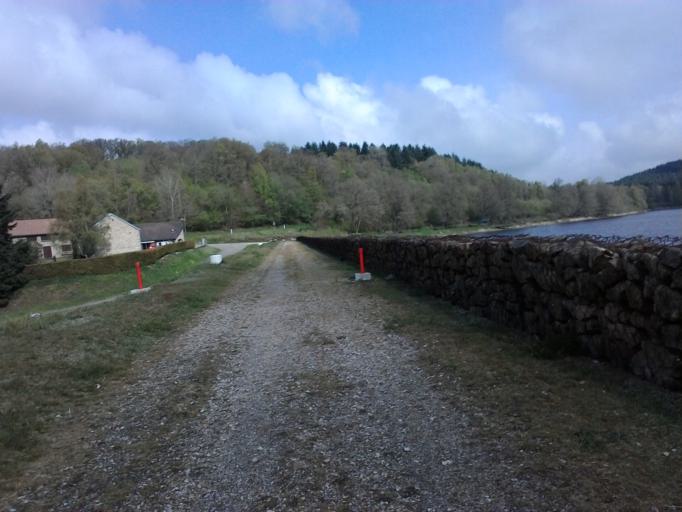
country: FR
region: Bourgogne
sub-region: Departement de la Cote-d'Or
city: Saulieu
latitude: 47.2446
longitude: 4.1885
